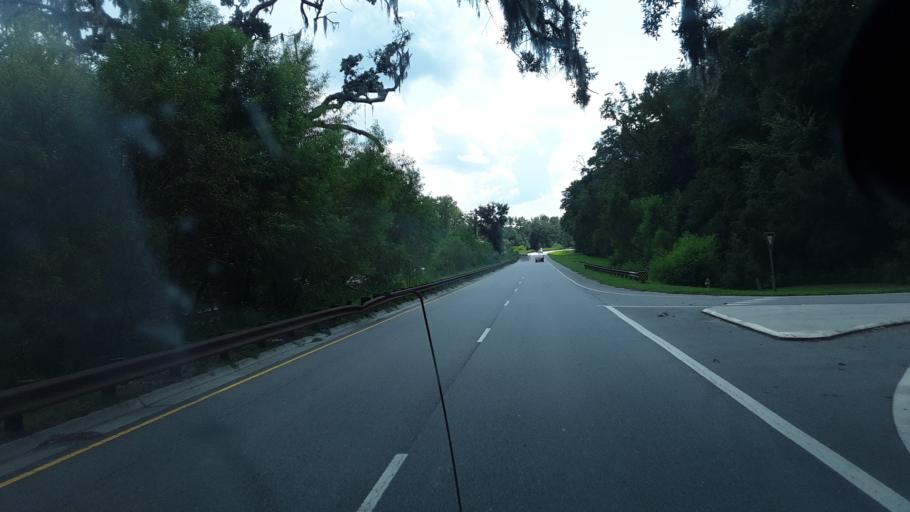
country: US
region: South Carolina
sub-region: Beaufort County
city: Bluffton
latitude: 32.2795
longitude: -80.9460
